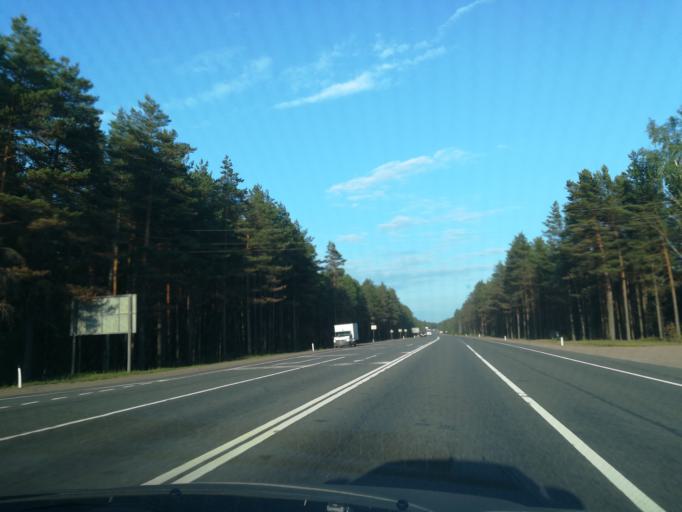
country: RU
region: Leningrad
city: Veshchevo
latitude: 60.6374
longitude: 29.0085
